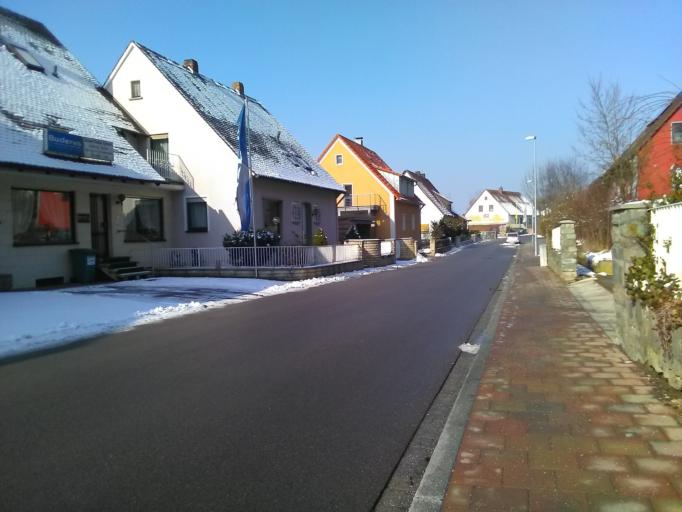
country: DE
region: Bavaria
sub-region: Regierungsbezirk Mittelfranken
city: Windsbach
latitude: 49.2504
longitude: 10.8265
